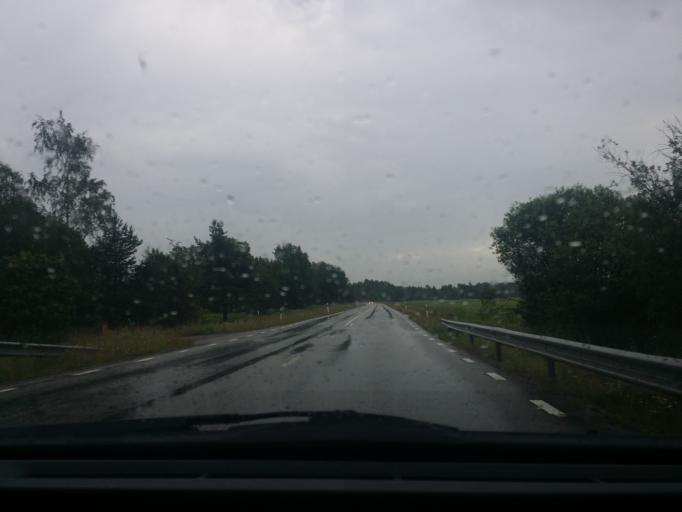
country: SE
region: OErebro
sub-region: Lindesbergs Kommun
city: Fellingsbro
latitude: 59.4555
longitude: 15.5782
